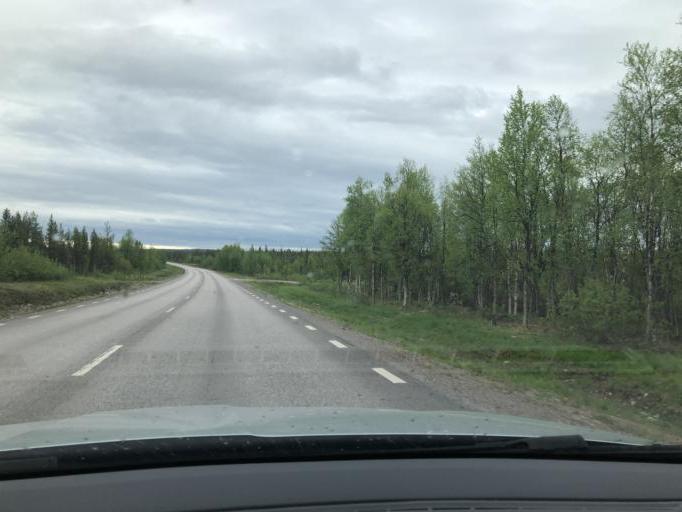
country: SE
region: Norrbotten
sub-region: Kiruna Kommun
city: Kiruna
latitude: 67.8042
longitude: 20.5905
